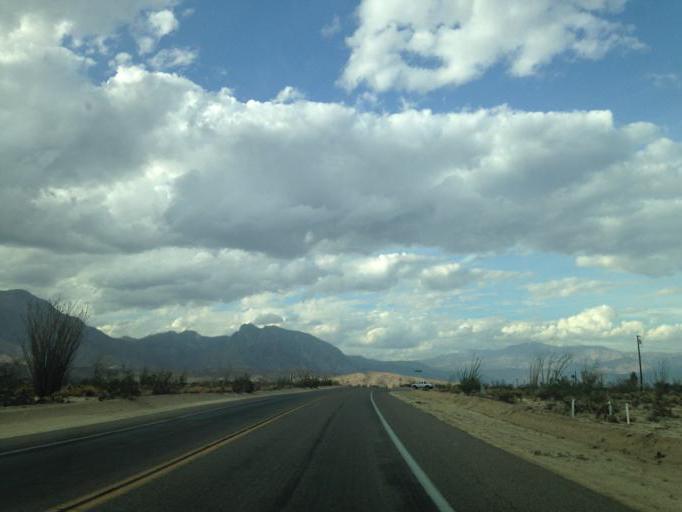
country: US
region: California
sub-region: San Diego County
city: Borrego Springs
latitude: 33.2196
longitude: -116.3731
